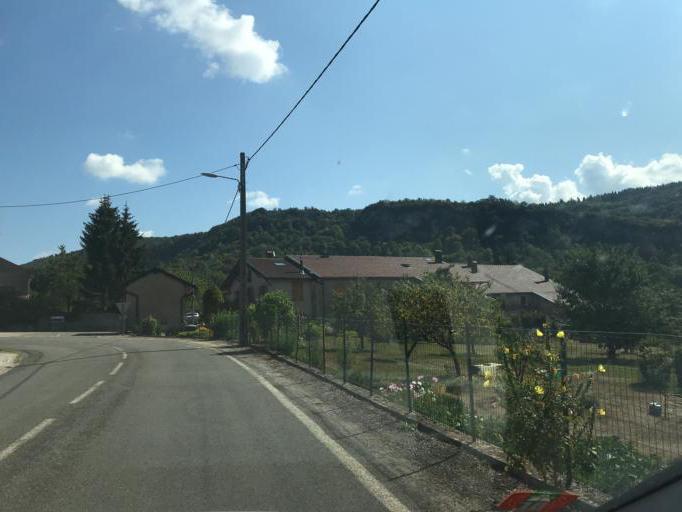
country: FR
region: Franche-Comte
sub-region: Departement du Jura
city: Moirans-en-Montagne
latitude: 46.4574
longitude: 5.7343
